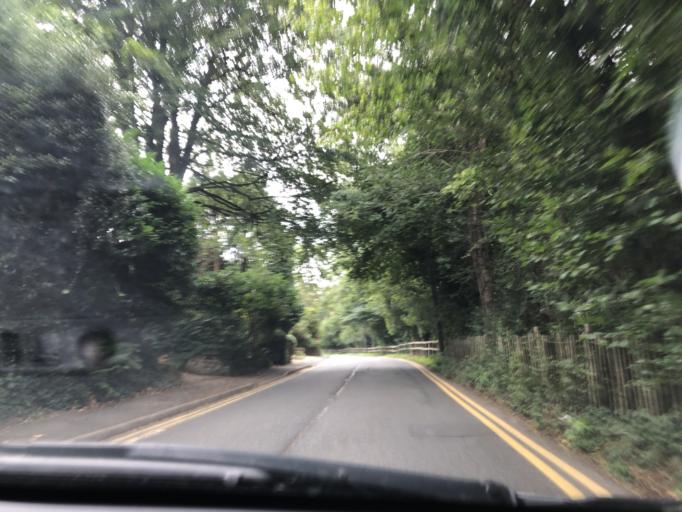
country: GB
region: England
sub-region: Kent
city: Westerham
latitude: 51.2641
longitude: 0.0779
